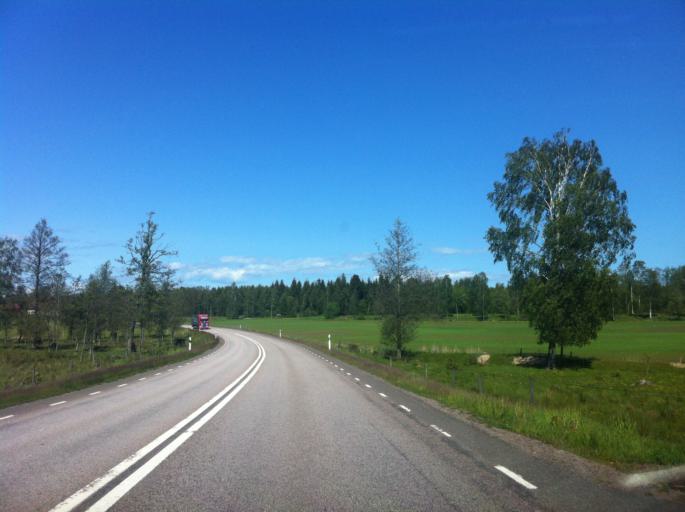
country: SE
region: Vaestra Goetaland
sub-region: Gullspangs Kommun
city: Gullspang
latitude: 58.9904
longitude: 14.0995
